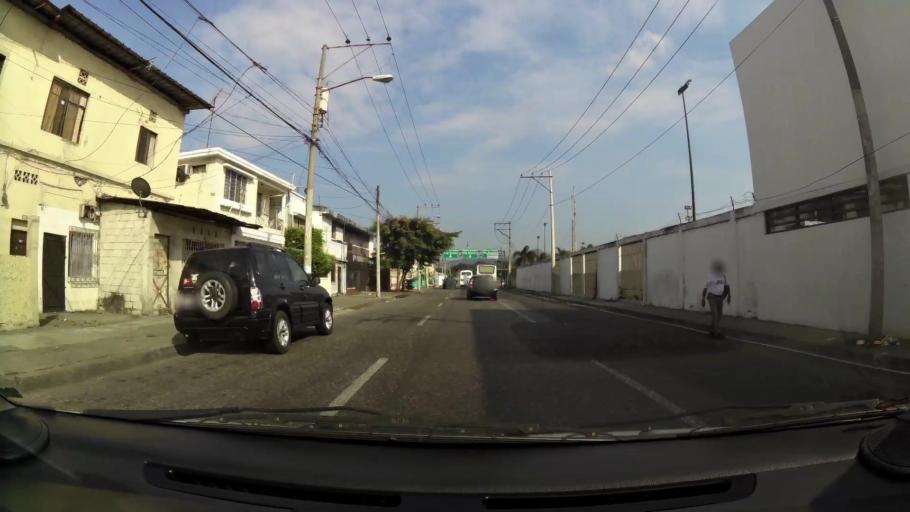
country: EC
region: Guayas
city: Guayaquil
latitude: -2.1899
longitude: -79.8995
